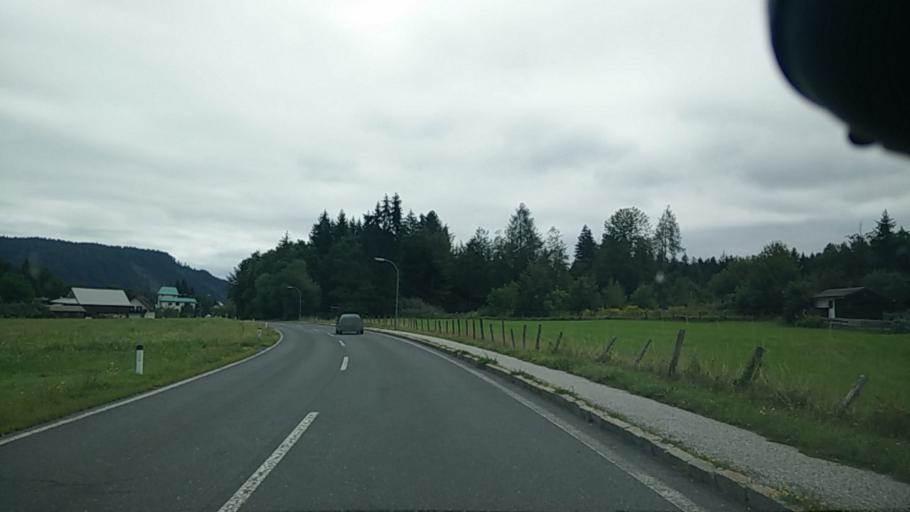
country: AT
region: Carinthia
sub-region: Politischer Bezirk Villach Land
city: Wernberg
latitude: 46.5561
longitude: 13.9514
